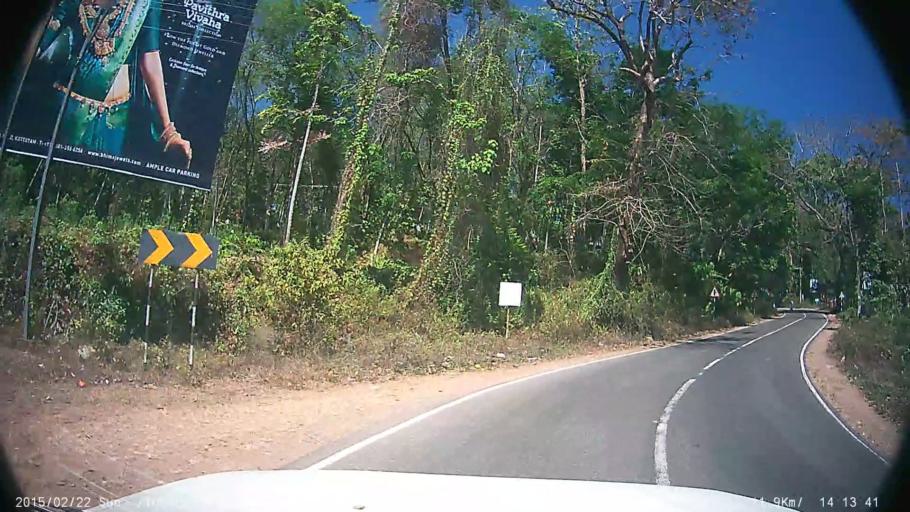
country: IN
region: Kerala
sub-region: Kottayam
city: Kottayam
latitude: 9.5402
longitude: 76.6819
